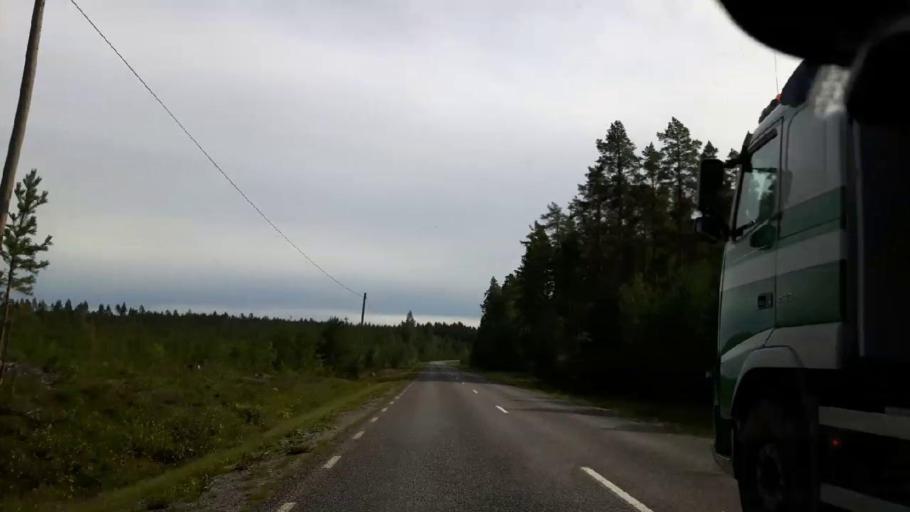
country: SE
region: Jaemtland
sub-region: Ragunda Kommun
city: Hammarstrand
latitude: 63.1458
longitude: 15.8510
